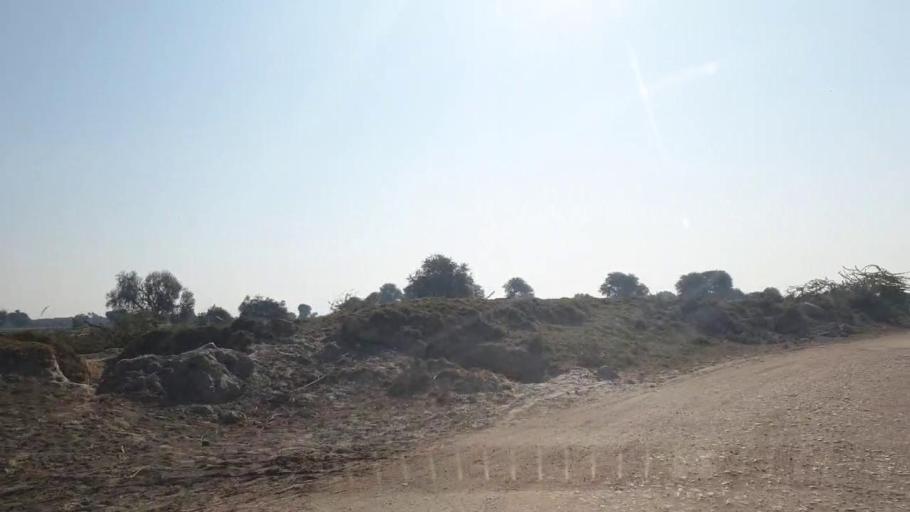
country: PK
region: Sindh
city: Shahpur Chakar
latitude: 26.0891
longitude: 68.6474
